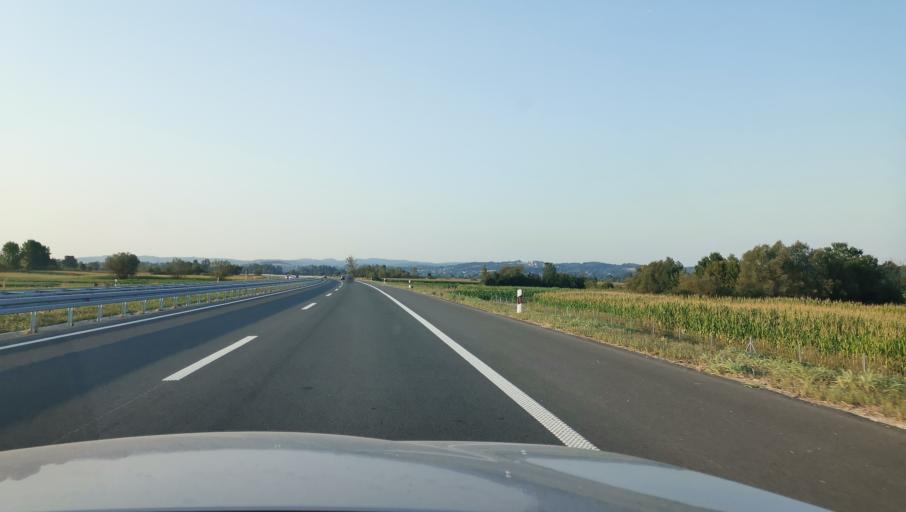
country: RS
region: Central Serbia
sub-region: Kolubarski Okrug
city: Ljig
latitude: 44.2533
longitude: 20.2701
